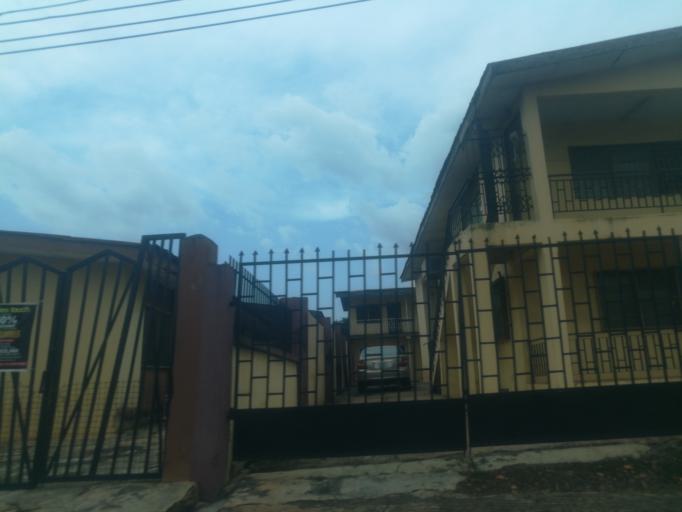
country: NG
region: Oyo
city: Ibadan
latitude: 7.3779
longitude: 3.8277
